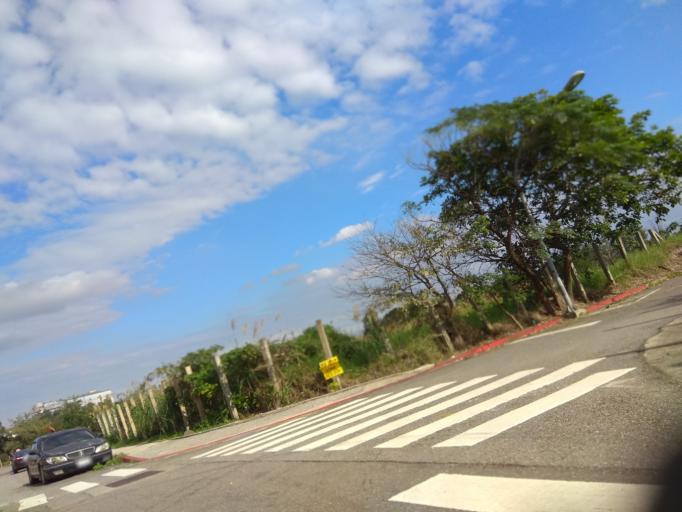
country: TW
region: Taiwan
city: Taoyuan City
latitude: 25.0544
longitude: 121.1791
